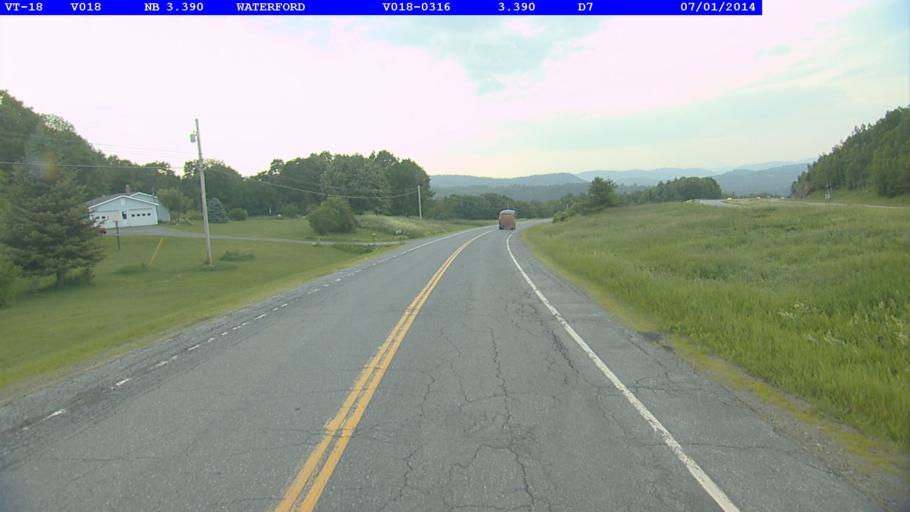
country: US
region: Vermont
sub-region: Caledonia County
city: Saint Johnsbury
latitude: 44.3808
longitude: -71.9222
